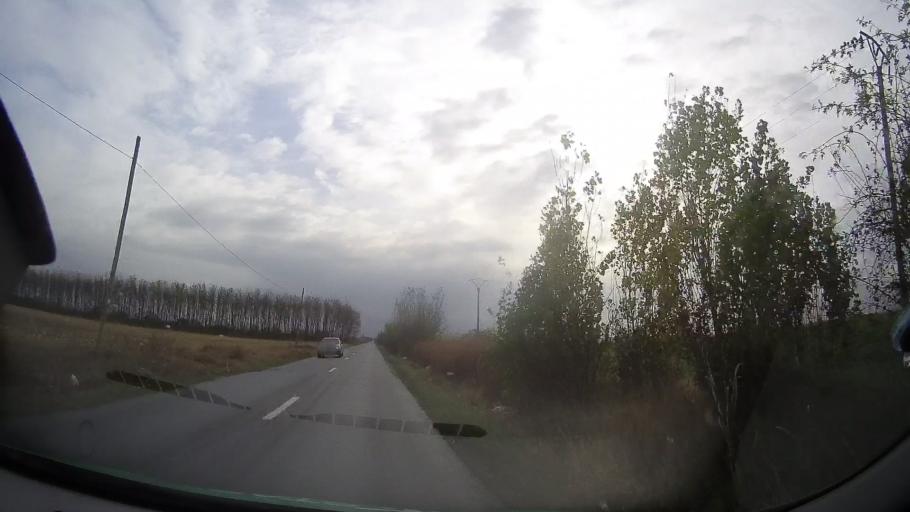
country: RO
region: Ialomita
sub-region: Comuna Fierbinti-Targ
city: Fierbintii de Jos
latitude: 44.7151
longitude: 26.3902
